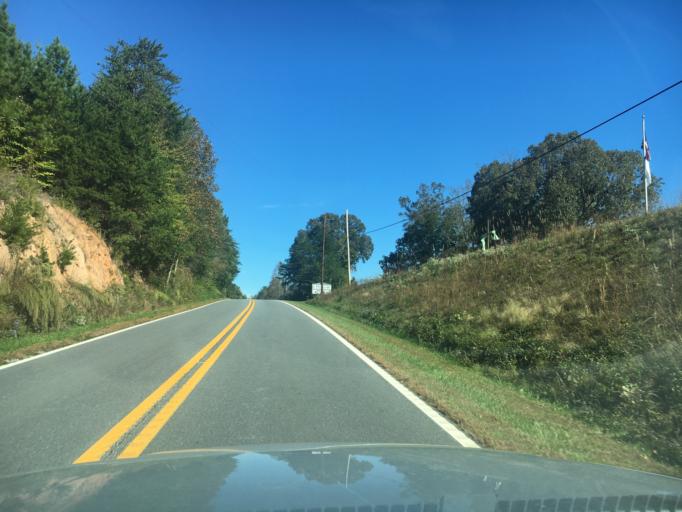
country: US
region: North Carolina
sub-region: Rutherford County
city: Spindale
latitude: 35.4770
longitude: -81.8812
